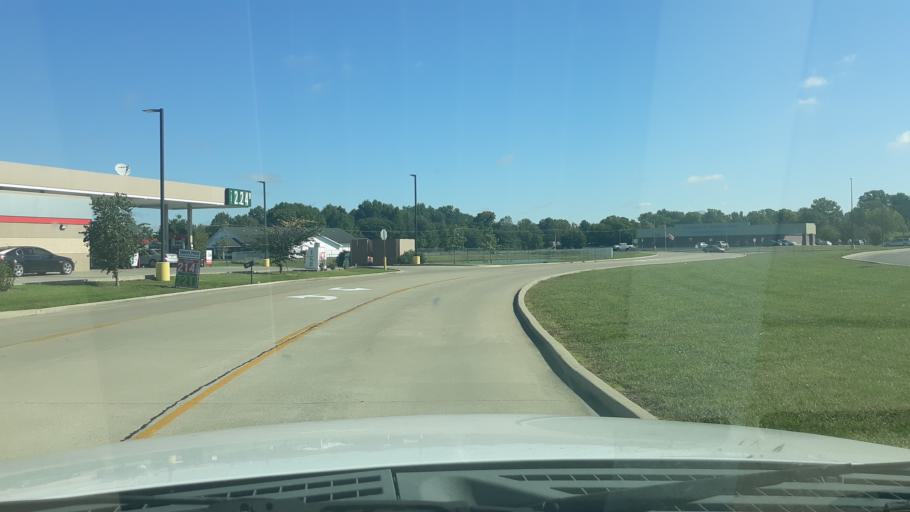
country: US
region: Illinois
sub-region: Saline County
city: Harrisburg
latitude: 37.7292
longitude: -88.5352
